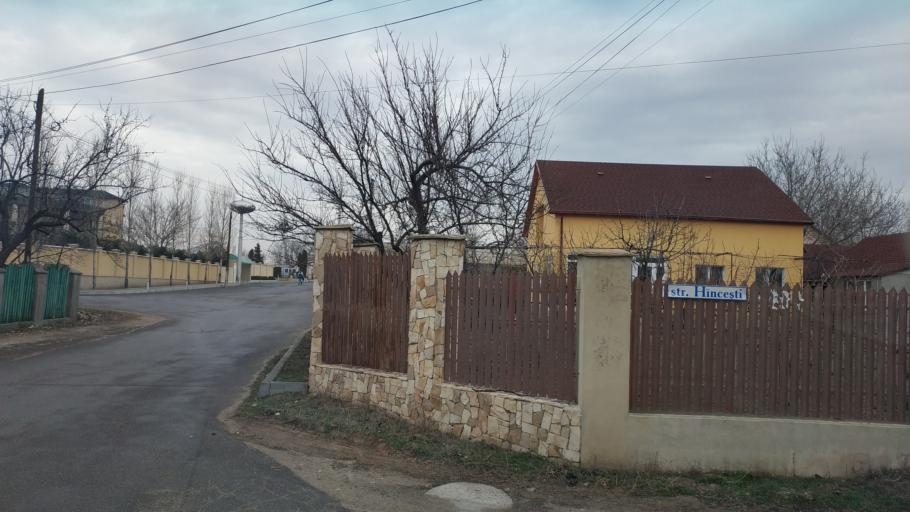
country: MD
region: Chisinau
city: Singera
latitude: 46.9200
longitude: 28.9620
